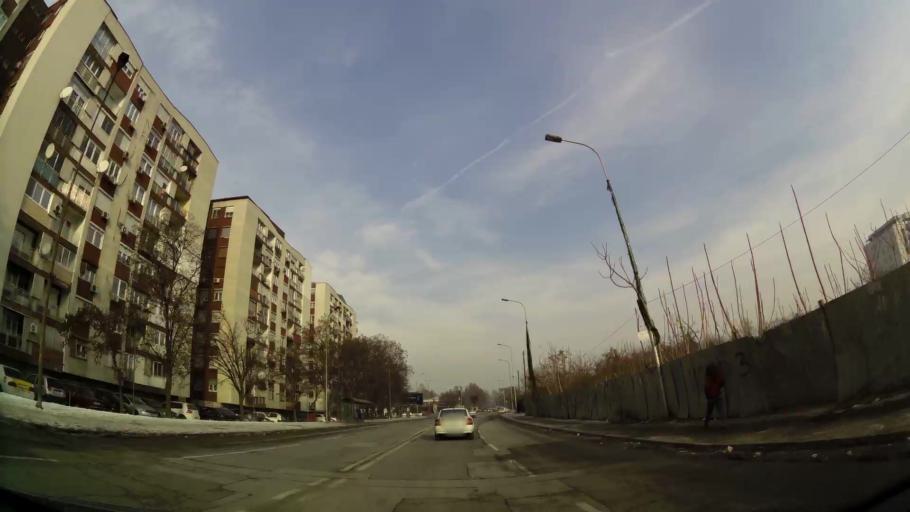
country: MK
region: Cair
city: Cair
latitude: 42.0211
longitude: 21.4341
